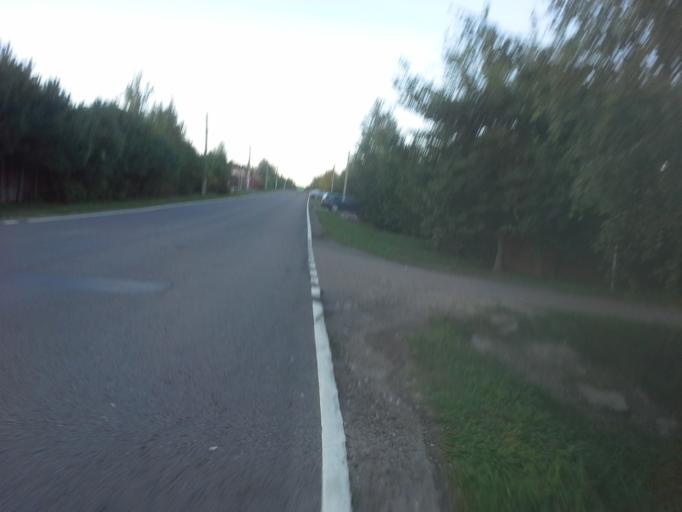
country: RU
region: Moskovskaya
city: Selyatino
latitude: 55.5050
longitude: 36.9323
